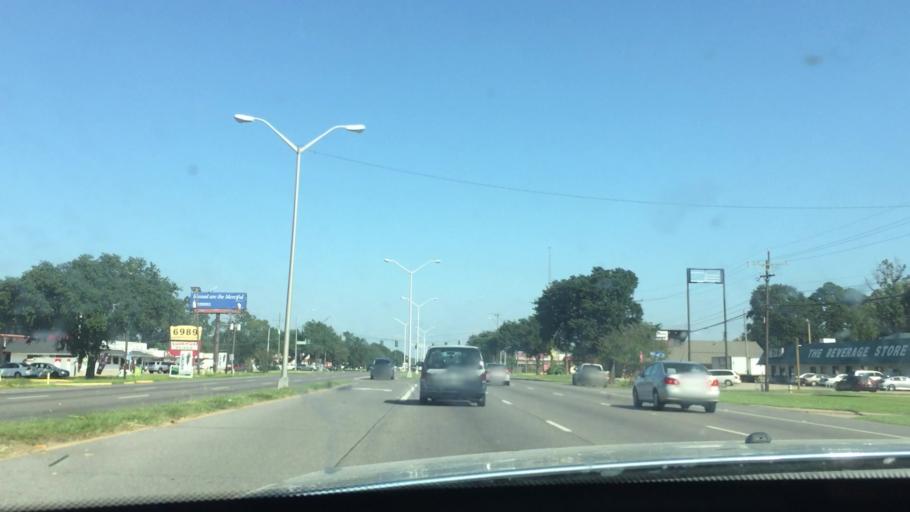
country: US
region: Louisiana
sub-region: East Baton Rouge Parish
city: Baton Rouge
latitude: 30.4514
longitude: -91.1204
